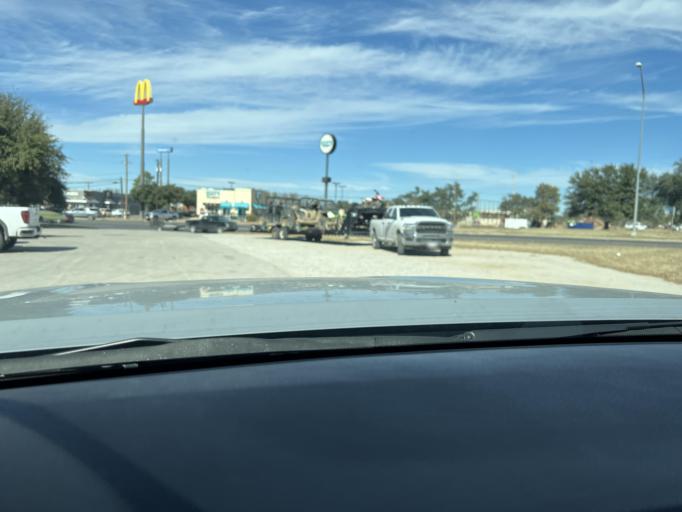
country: US
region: Texas
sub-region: Eastland County
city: Eastland
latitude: 32.4010
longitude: -98.7908
